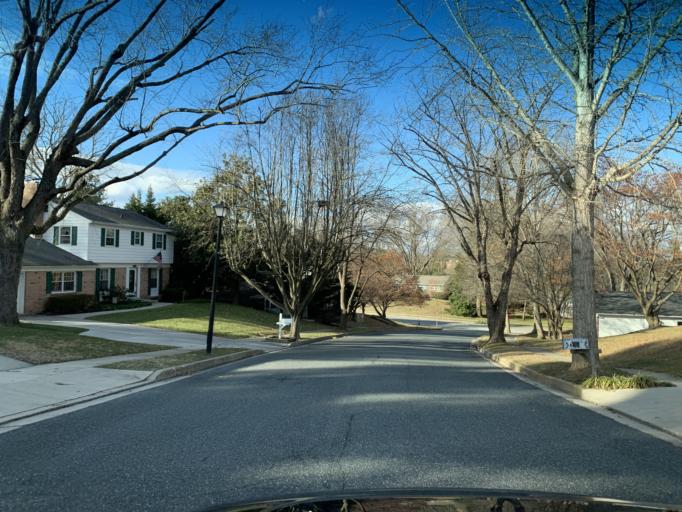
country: US
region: Maryland
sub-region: Harford County
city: South Bel Air
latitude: 39.5338
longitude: -76.3311
